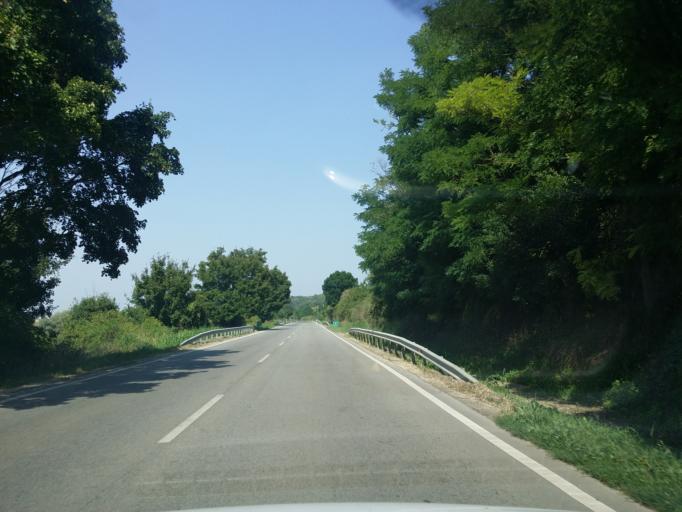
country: HU
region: Tolna
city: Pincehely
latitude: 46.6985
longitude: 18.4656
